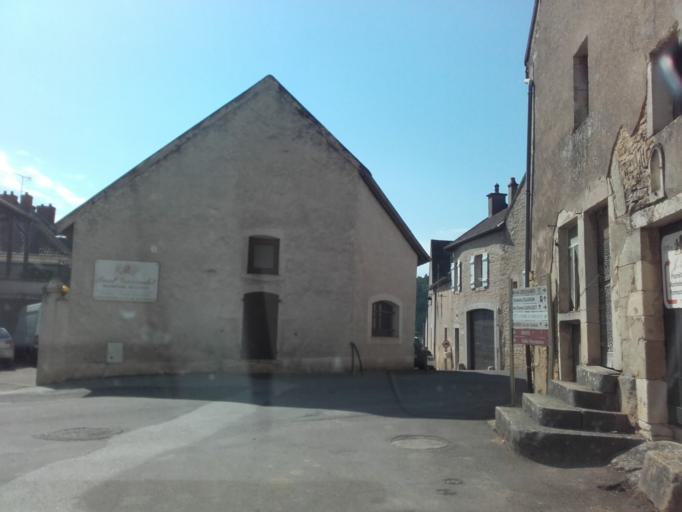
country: FR
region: Bourgogne
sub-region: Departement de la Cote-d'Or
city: Meursault
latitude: 46.9931
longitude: 4.7673
